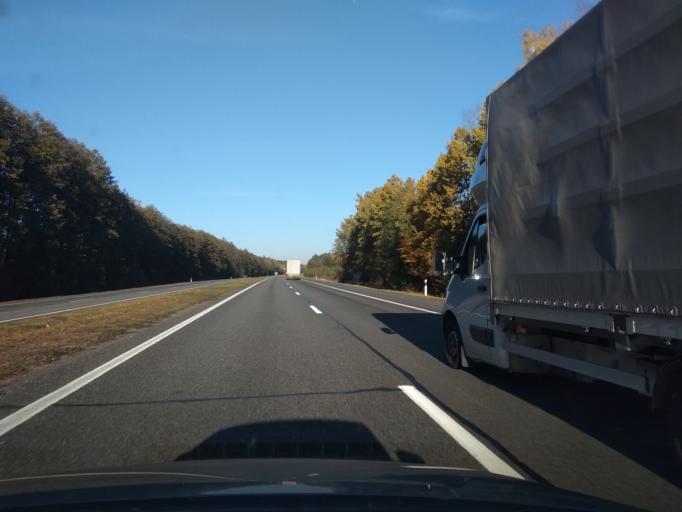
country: BY
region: Brest
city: Nyakhachava
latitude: 52.6441
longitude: 25.2381
